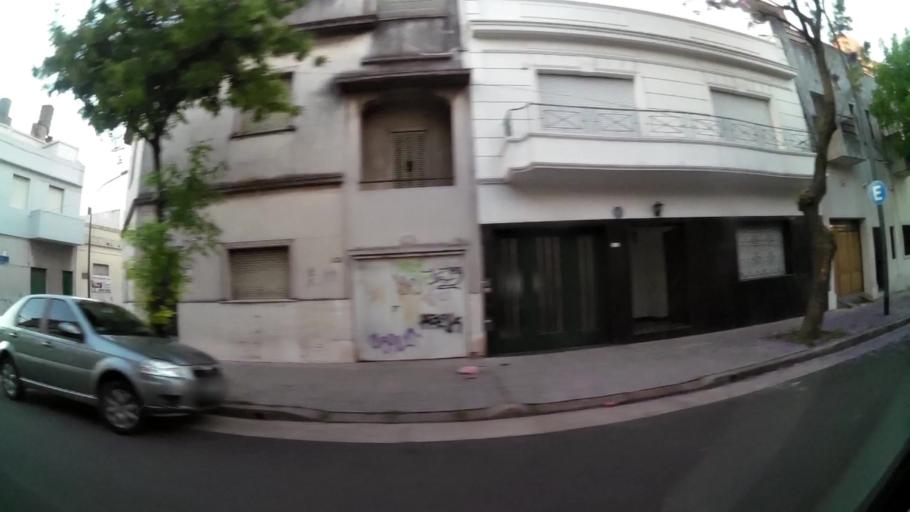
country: AR
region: Buenos Aires F.D.
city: Villa Santa Rita
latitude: -34.6374
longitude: -58.4400
